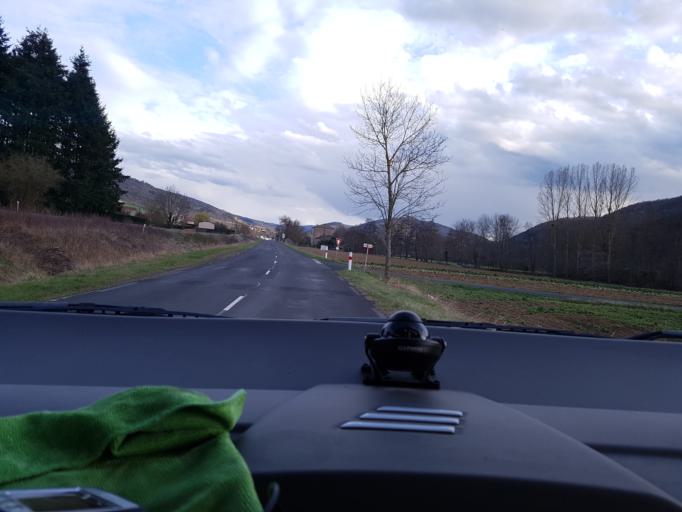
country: FR
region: Auvergne
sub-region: Departement du Cantal
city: Massiac
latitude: 45.2711
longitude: 3.1934
